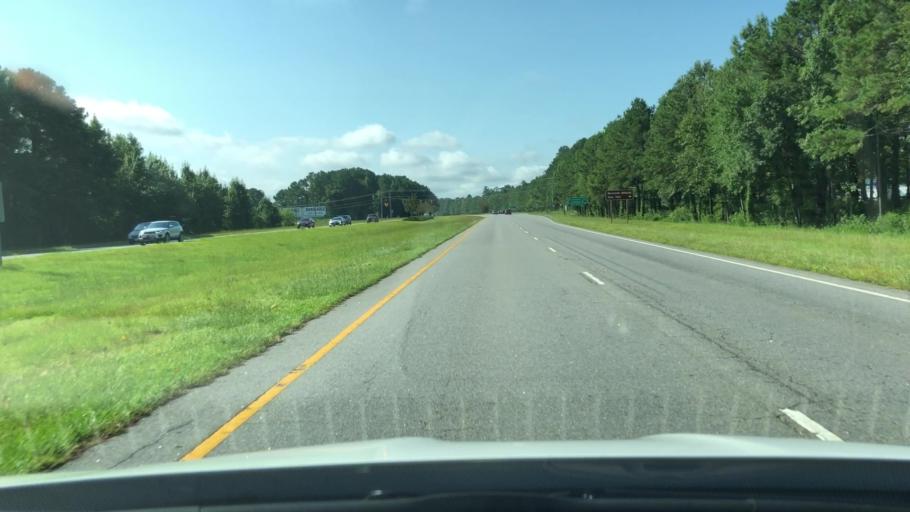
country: US
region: North Carolina
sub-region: Pasquotank County
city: Elizabeth City
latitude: 36.4171
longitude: -76.3416
